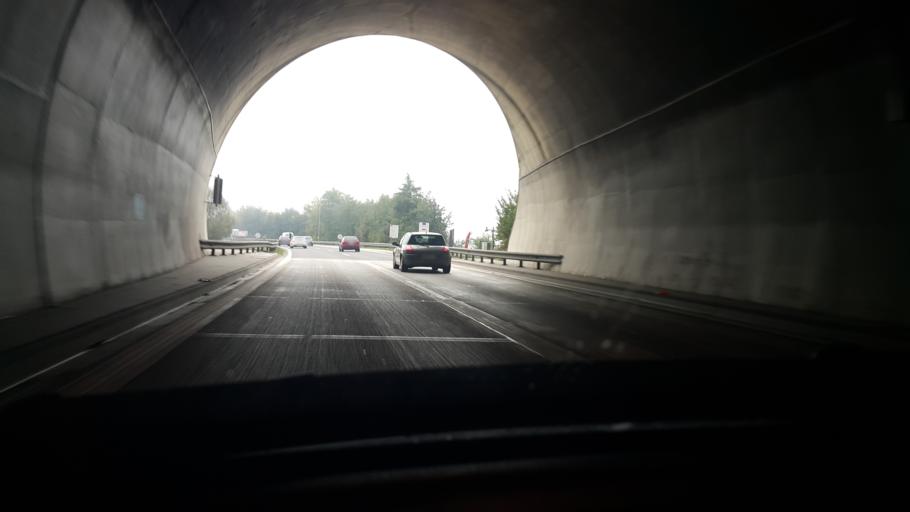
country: SI
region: Skofljica
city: Lavrica
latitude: 46.0079
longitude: 14.5671
